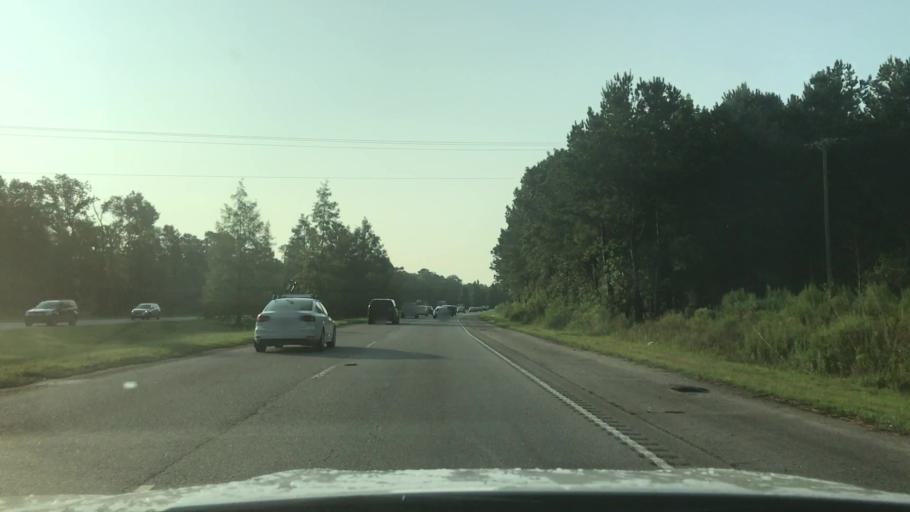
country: US
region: South Carolina
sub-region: Charleston County
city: Shell Point
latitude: 32.8184
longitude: -80.0658
